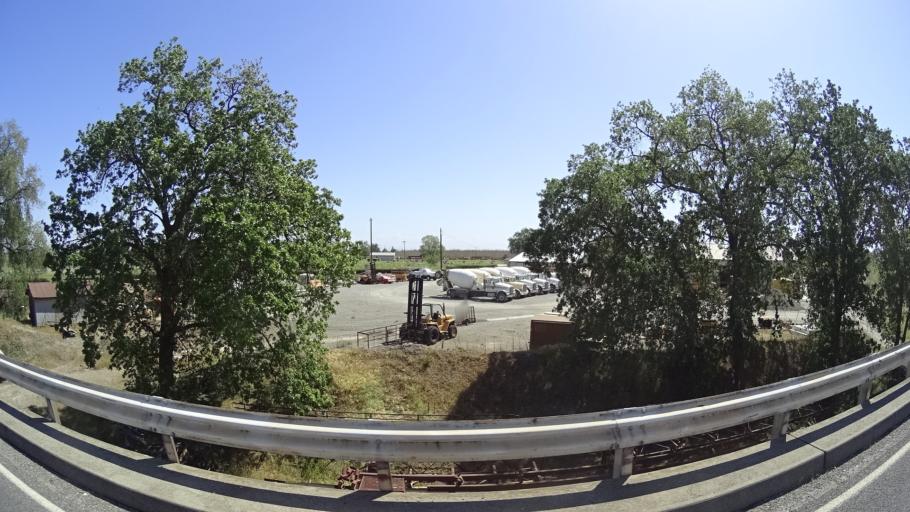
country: US
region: California
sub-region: Glenn County
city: Orland
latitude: 39.7681
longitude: -122.1967
